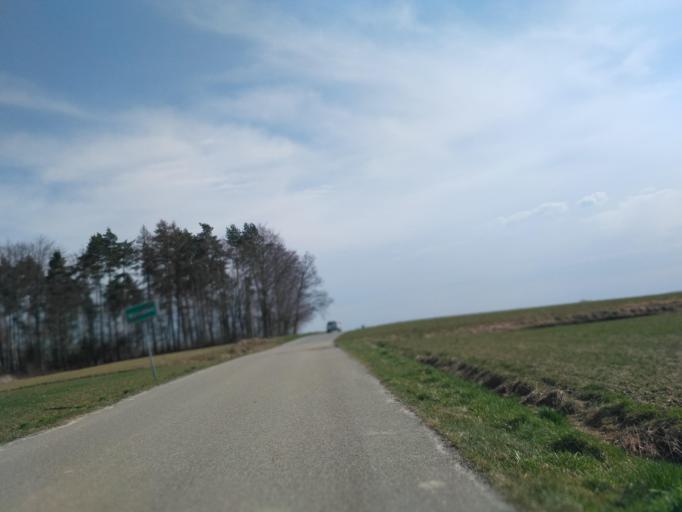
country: PL
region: Subcarpathian Voivodeship
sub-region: Powiat ropczycko-sedziszowski
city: Iwierzyce
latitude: 49.9719
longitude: 21.7544
